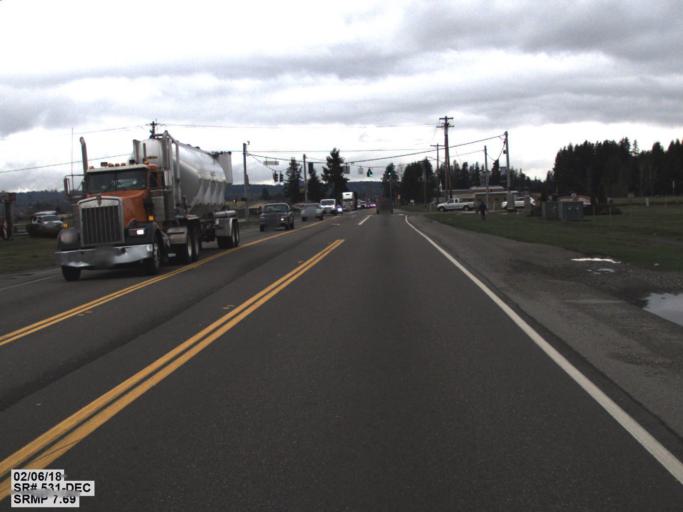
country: US
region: Washington
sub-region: Snohomish County
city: Smokey Point
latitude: 48.1521
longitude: -122.1601
